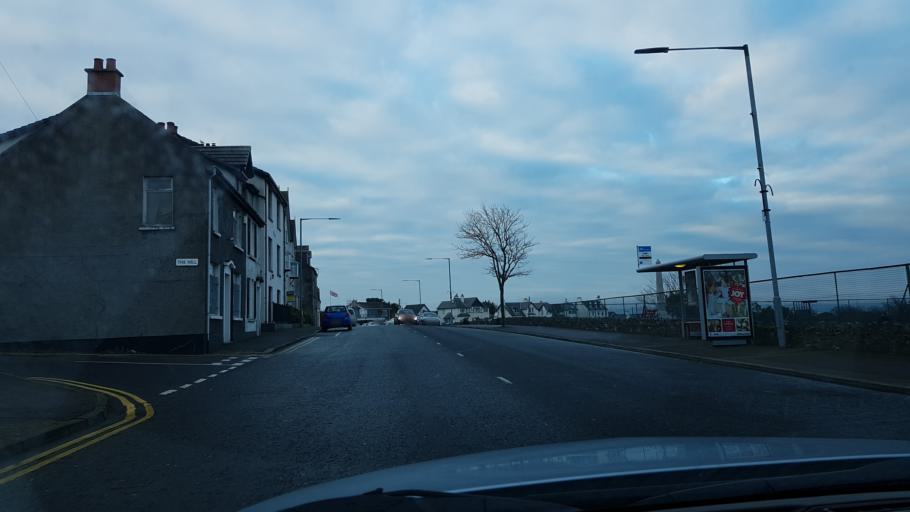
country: GB
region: Northern Ireland
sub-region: North Down District
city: Bangor
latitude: 54.6758
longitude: -5.6185
